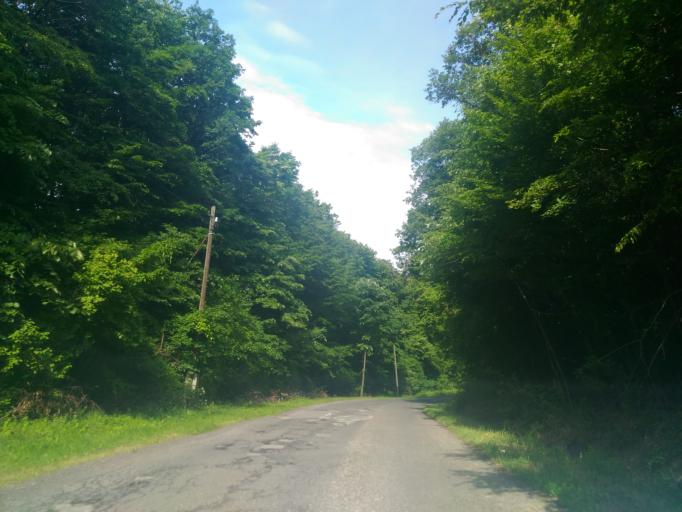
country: HU
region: Baranya
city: Pecs
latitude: 46.1344
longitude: 18.2490
